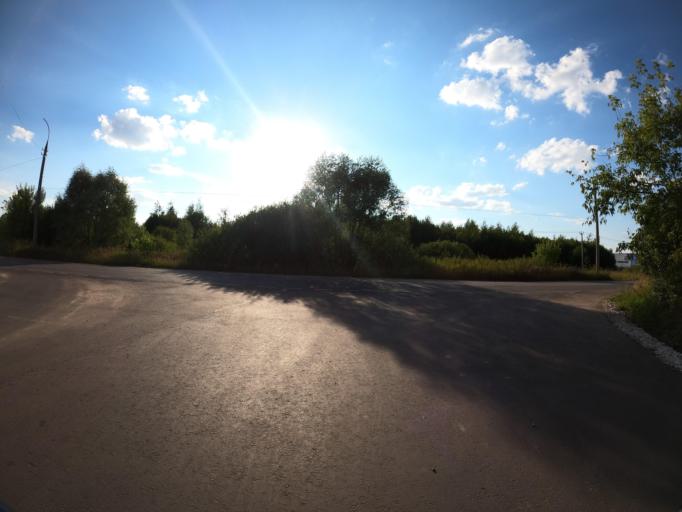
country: RU
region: Moskovskaya
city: Raduzhnyy
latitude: 55.1502
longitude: 38.7308
